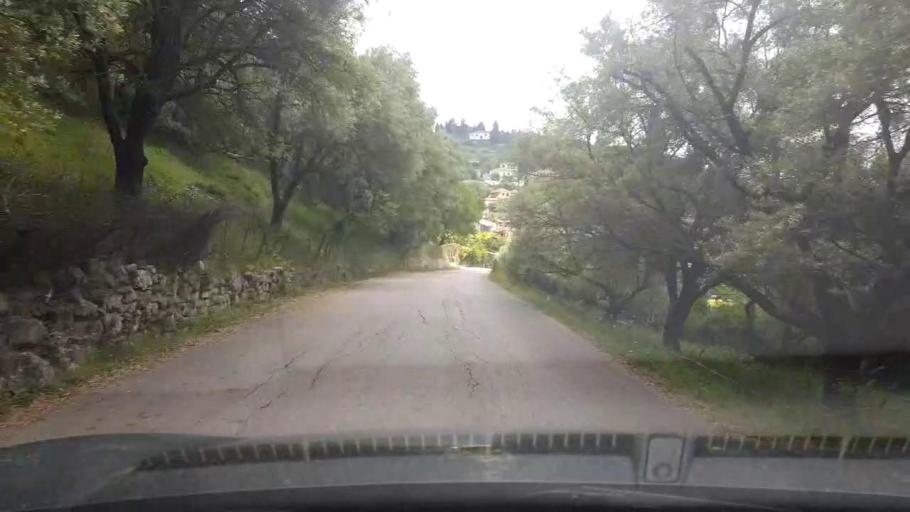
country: GR
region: Ionian Islands
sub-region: Lefkada
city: Nidri
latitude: 38.6444
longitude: 20.7072
